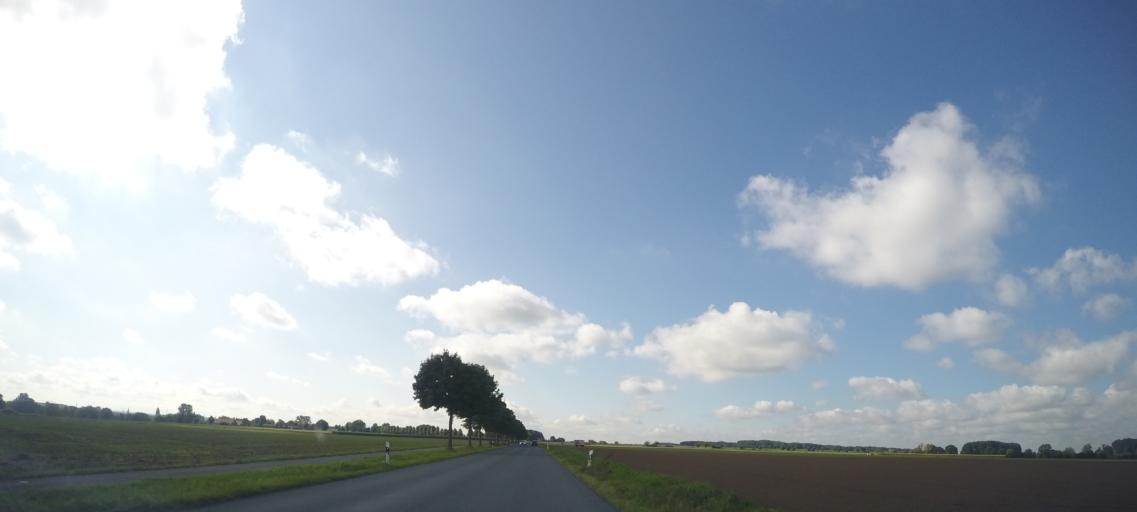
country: DE
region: North Rhine-Westphalia
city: Erwitte
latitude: 51.6427
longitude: 8.3234
